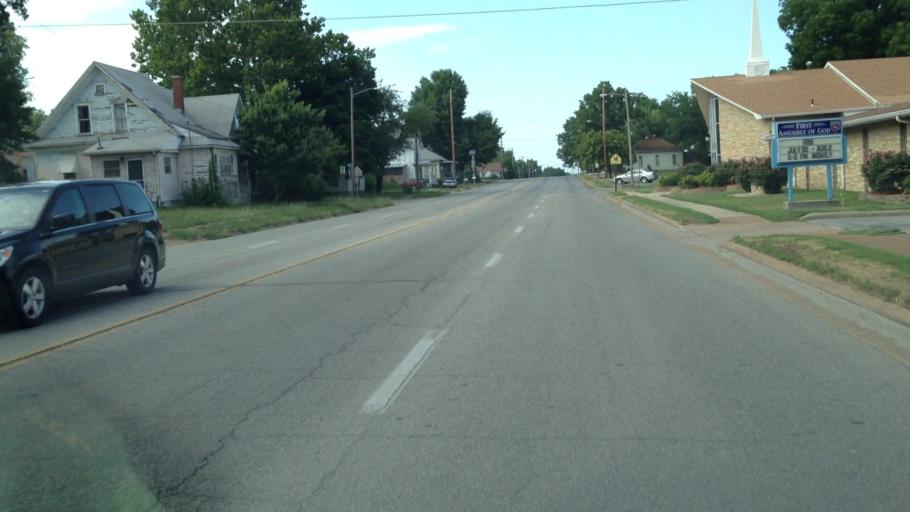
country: US
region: Kansas
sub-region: Labette County
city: Parsons
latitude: 37.3450
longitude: -95.2591
